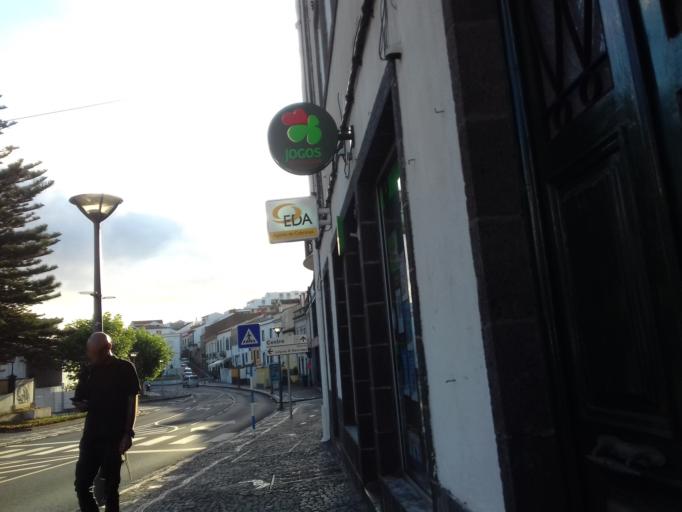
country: PT
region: Azores
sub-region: Ponta Delgada
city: Rosto de Cao
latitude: 37.7427
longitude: -25.6573
